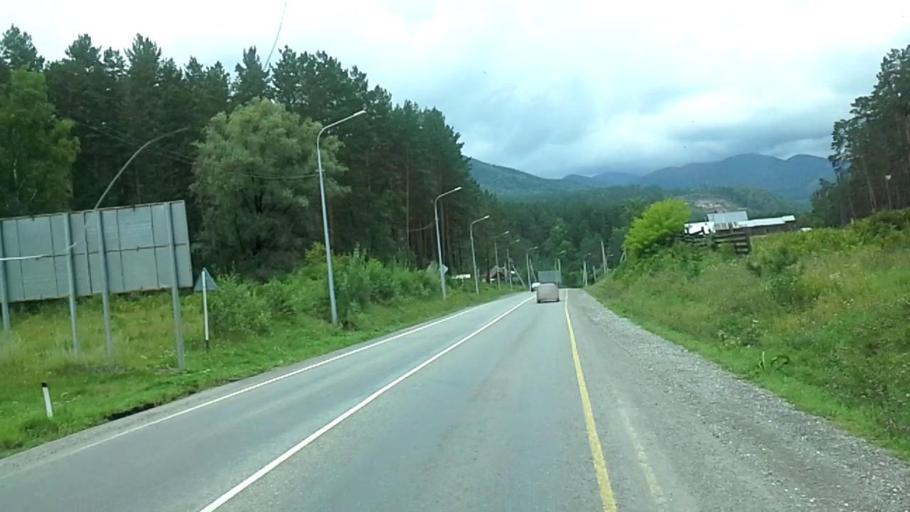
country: RU
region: Altay
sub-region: Mayminskiy Rayon
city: Manzherok
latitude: 51.8211
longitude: 85.7856
